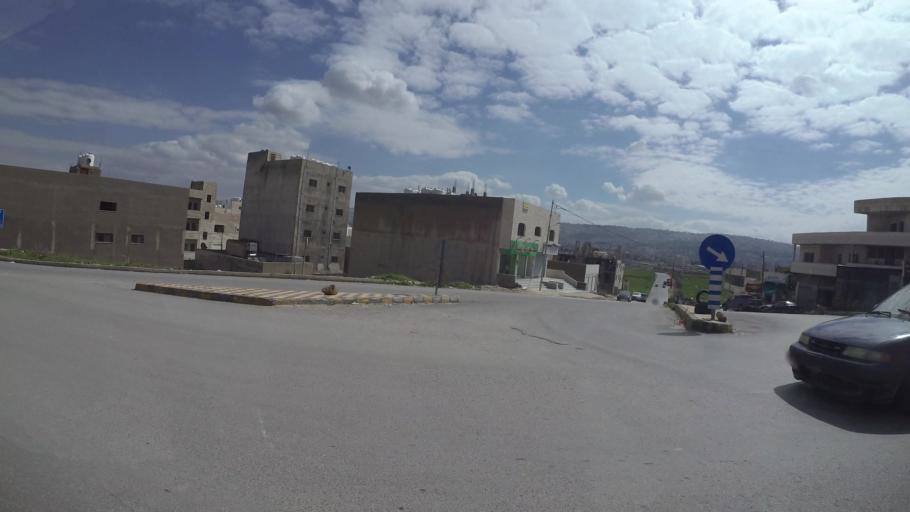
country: JO
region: Amman
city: Al Jubayhah
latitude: 32.0686
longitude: 35.8157
